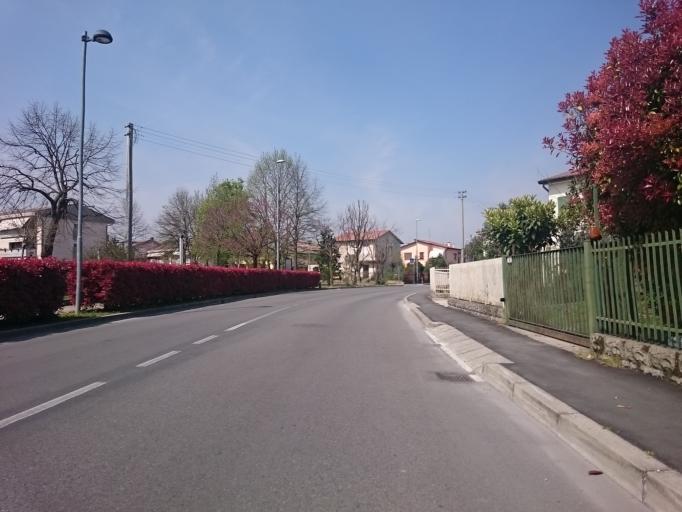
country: IT
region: Veneto
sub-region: Provincia di Padova
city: Tencarola
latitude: 45.3959
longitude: 11.8064
